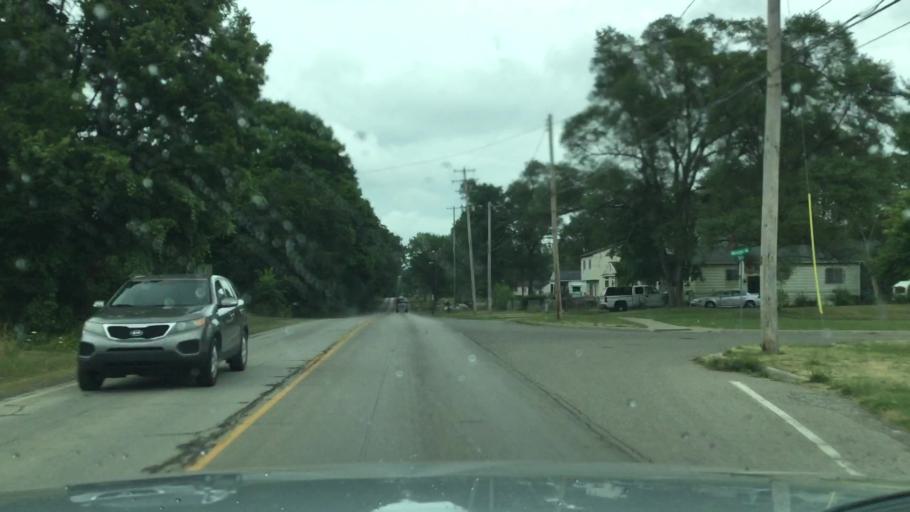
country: US
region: Michigan
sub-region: Genesee County
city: Beecher
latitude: 43.0761
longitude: -83.6662
